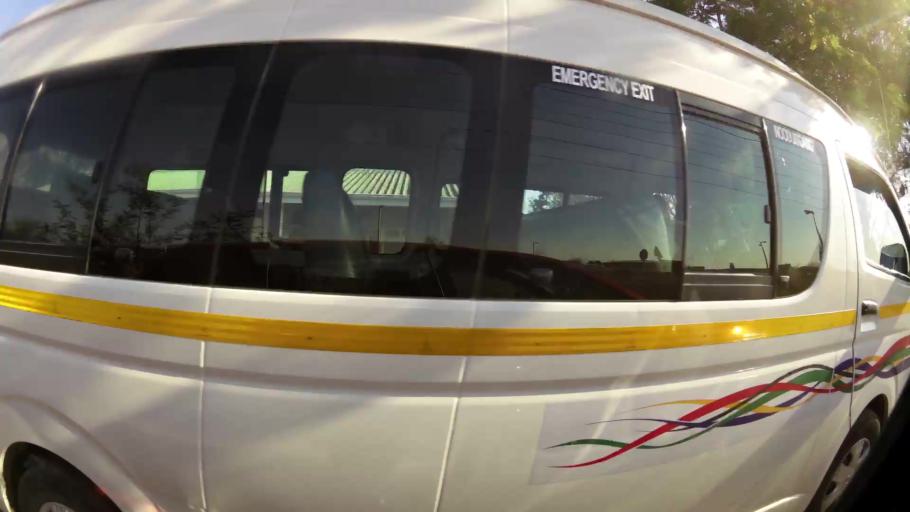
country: ZA
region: North-West
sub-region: Bojanala Platinum District Municipality
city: Rustenburg
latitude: -25.6503
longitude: 27.2383
